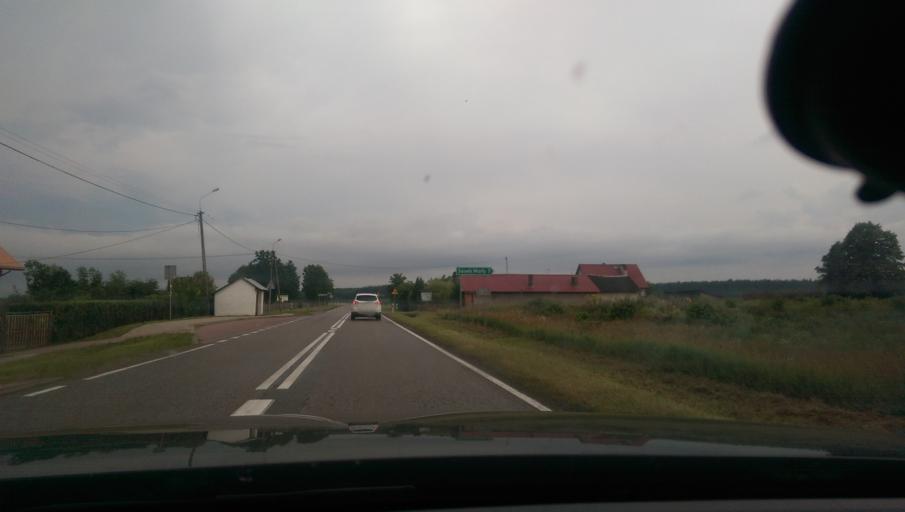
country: PL
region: Warmian-Masurian Voivodeship
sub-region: Powiat szczycienski
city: Szczytno
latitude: 53.5044
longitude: 20.9672
